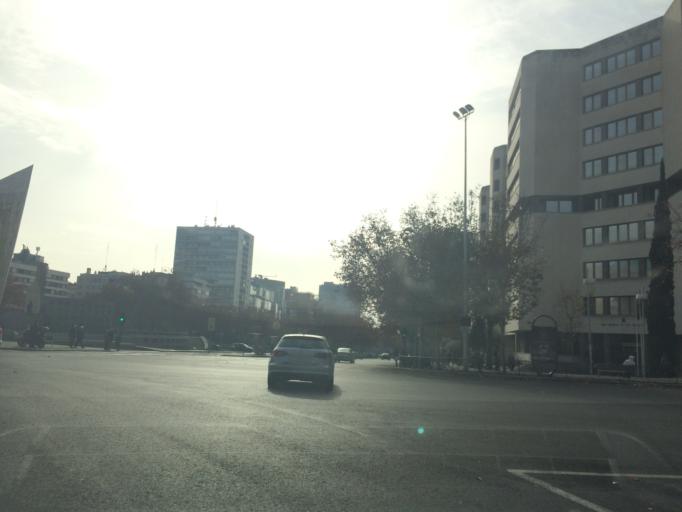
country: ES
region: Madrid
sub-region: Provincia de Madrid
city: Chamartin
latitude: 40.4659
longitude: -3.6899
